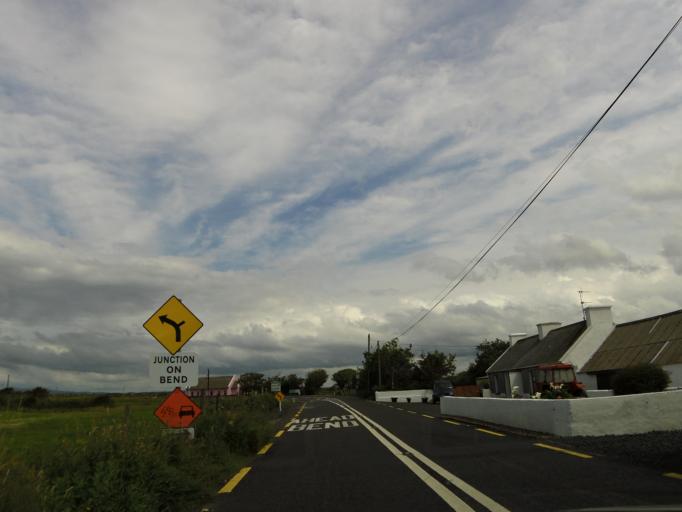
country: IE
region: Munster
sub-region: An Clar
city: Kilrush
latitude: 52.7372
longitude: -9.4848
